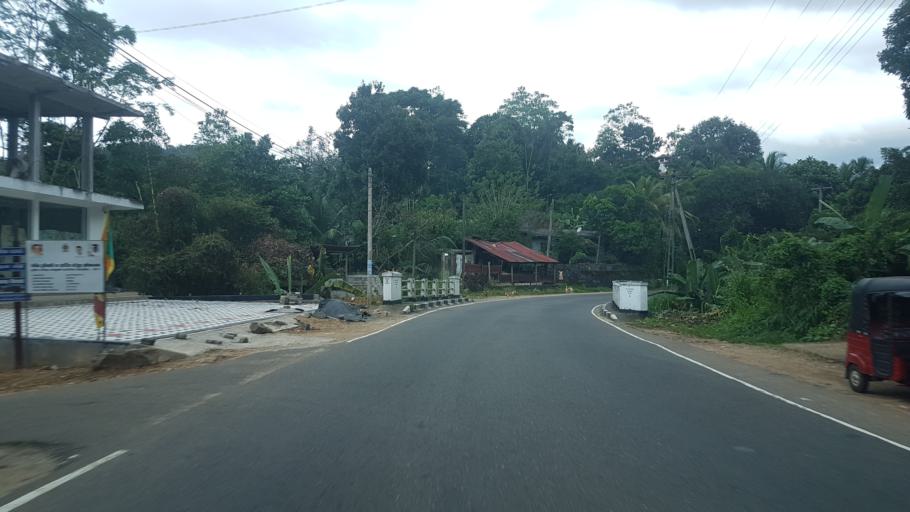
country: LK
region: Western
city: Hanwella Ihala
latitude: 7.0287
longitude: 80.2810
